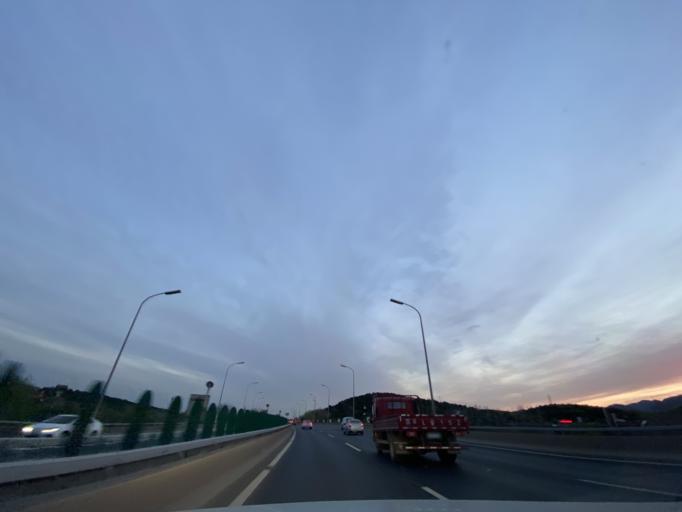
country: CN
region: Beijing
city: Haidian
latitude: 40.0084
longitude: 116.2661
